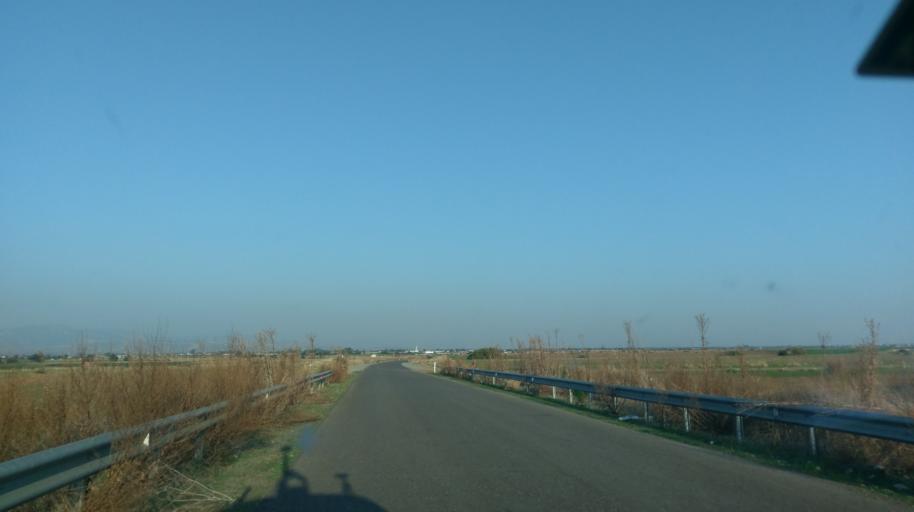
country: CY
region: Lefkosia
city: Morfou
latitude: 35.1506
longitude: 32.9815
